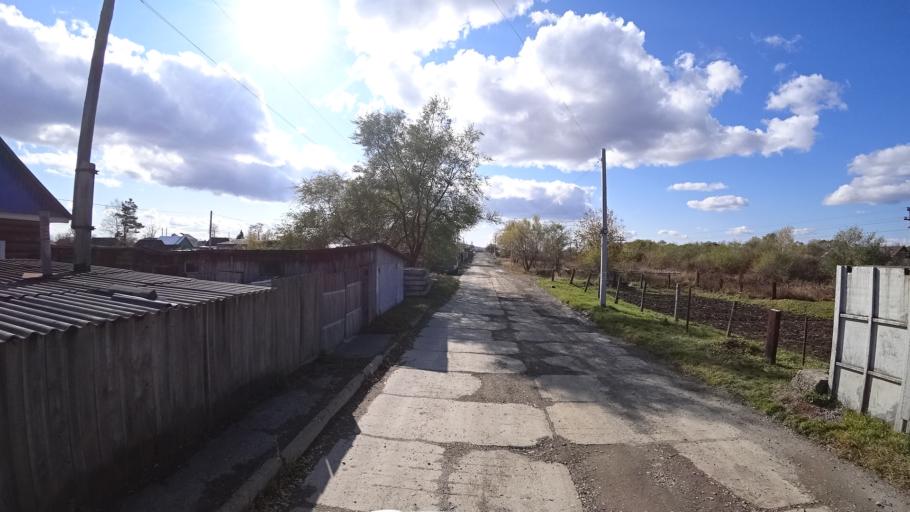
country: RU
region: Khabarovsk Krai
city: Amursk
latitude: 50.0960
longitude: 136.5048
